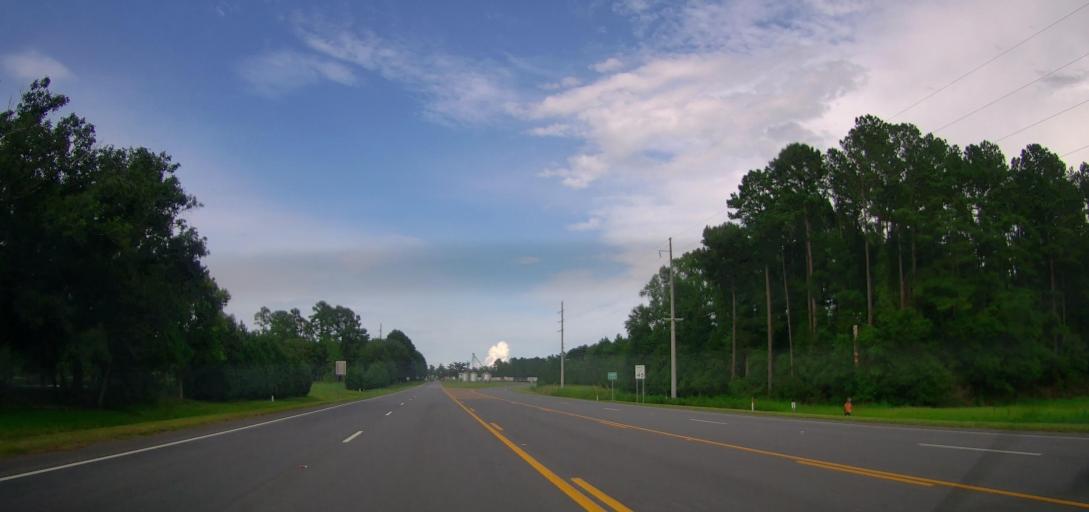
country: US
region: Georgia
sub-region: Wayne County
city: Jesup
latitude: 31.4787
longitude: -82.0272
